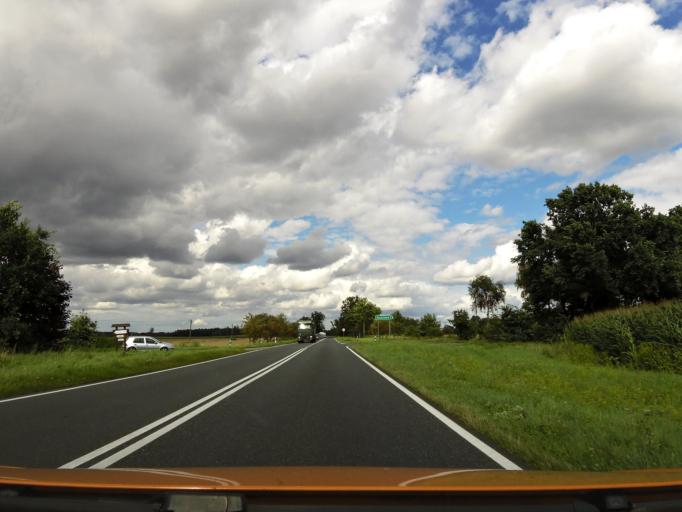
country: PL
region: West Pomeranian Voivodeship
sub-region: Powiat gryficki
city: Ploty
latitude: 53.7452
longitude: 15.2153
